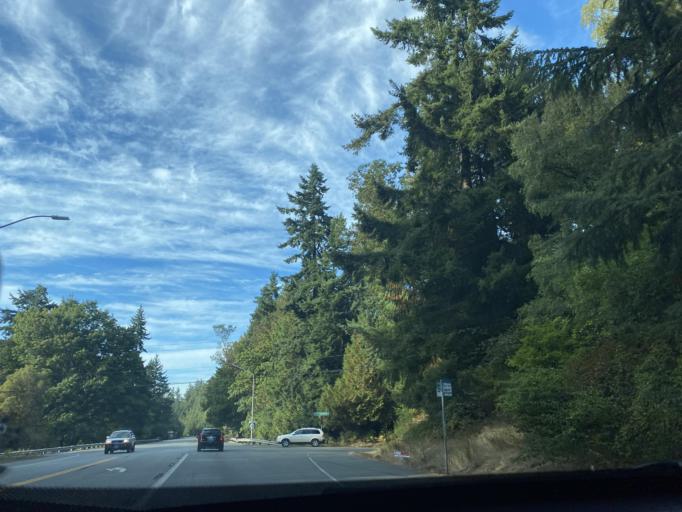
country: US
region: Washington
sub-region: Kitsap County
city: Suquamish
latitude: 47.7003
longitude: -122.5572
